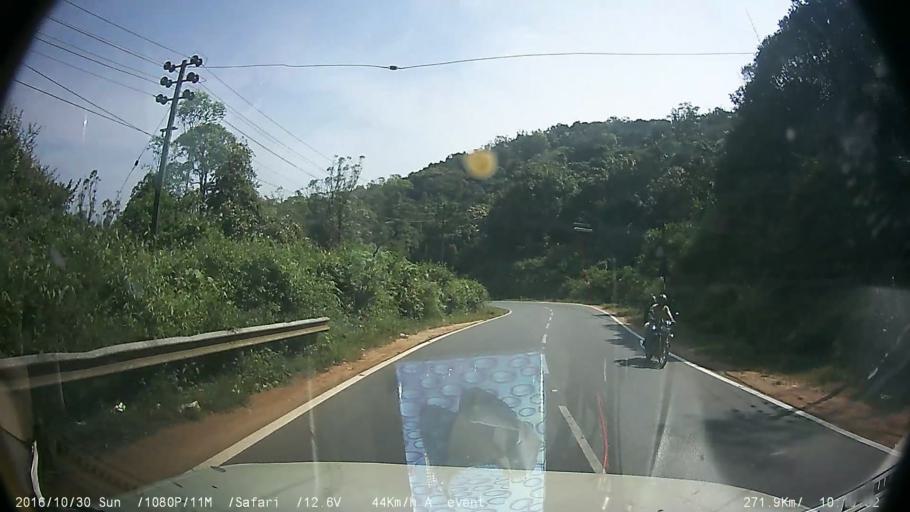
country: IN
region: Karnataka
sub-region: Kodagu
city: Madikeri
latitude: 12.4276
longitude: 75.7530
